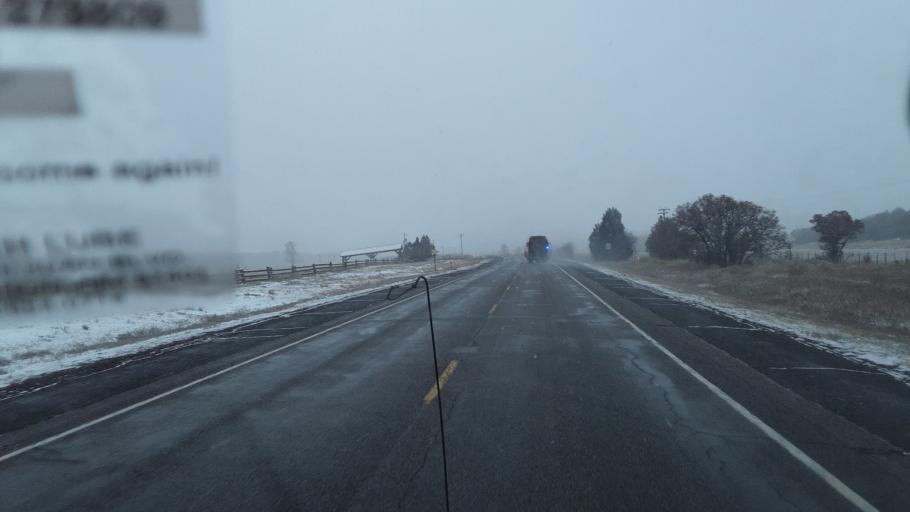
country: US
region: New Mexico
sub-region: Rio Arriba County
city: Chama
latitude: 36.8252
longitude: -106.5692
